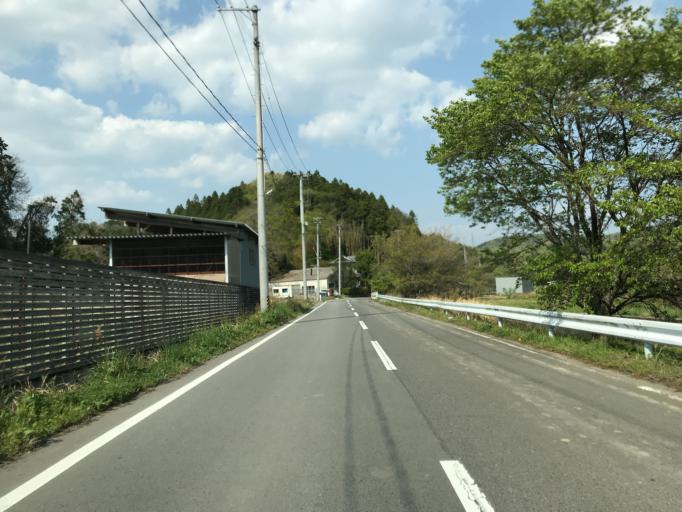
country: JP
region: Fukushima
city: Iwaki
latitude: 36.9672
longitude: 140.7572
